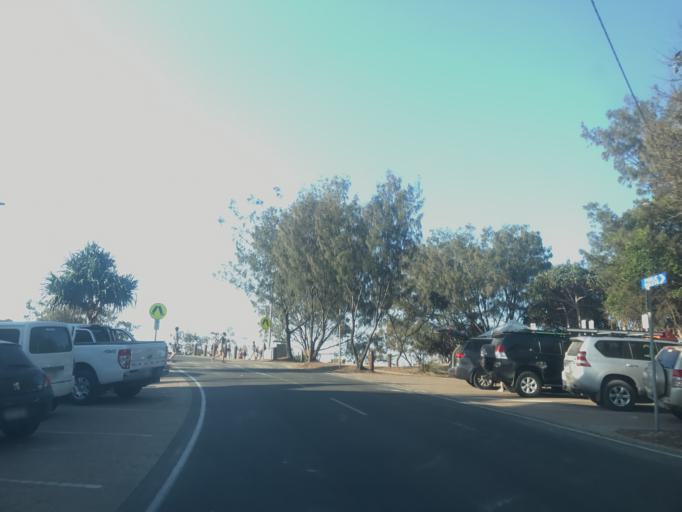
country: AU
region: Queensland
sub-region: Redland
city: Victoria Point
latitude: -27.4334
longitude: 153.5438
